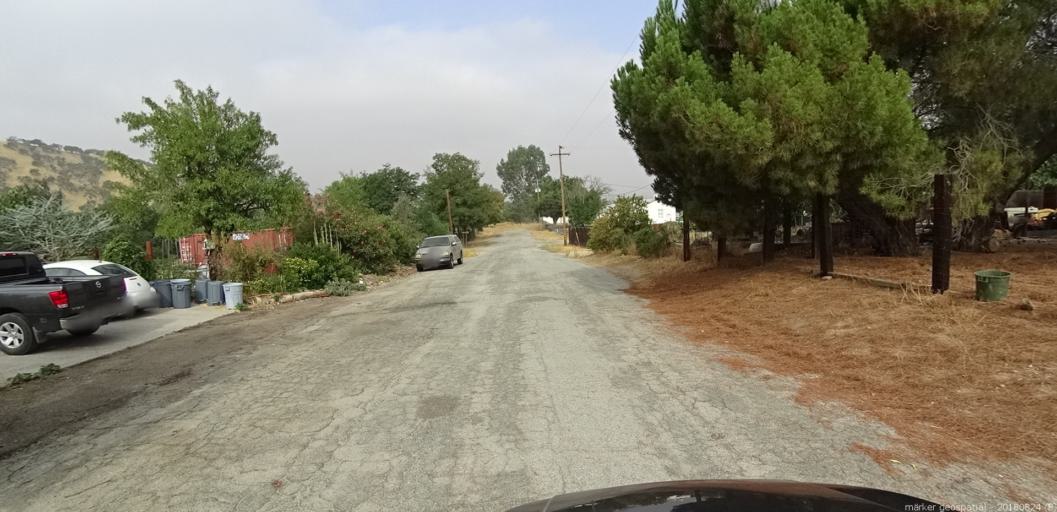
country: US
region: California
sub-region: San Luis Obispo County
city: San Miguel
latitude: 35.8621
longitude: -120.8039
